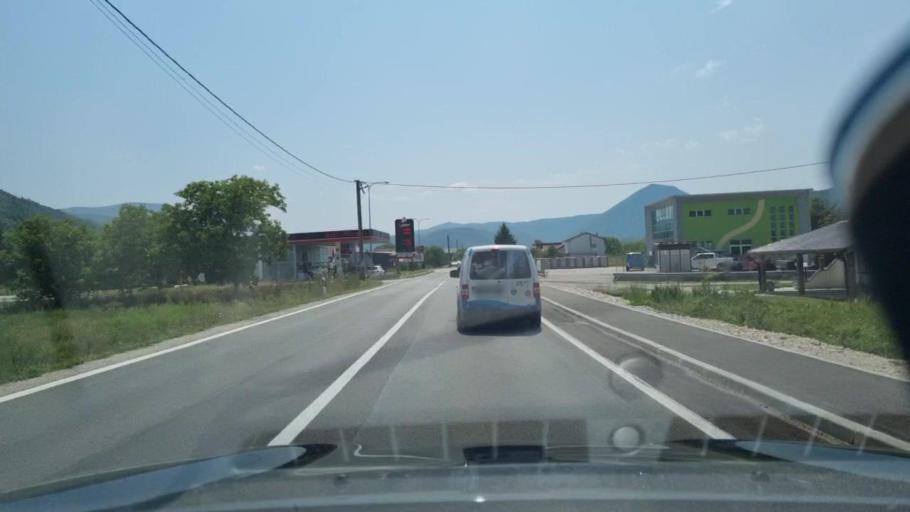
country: BA
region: Federation of Bosnia and Herzegovina
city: Bihac
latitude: 44.7904
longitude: 15.9289
